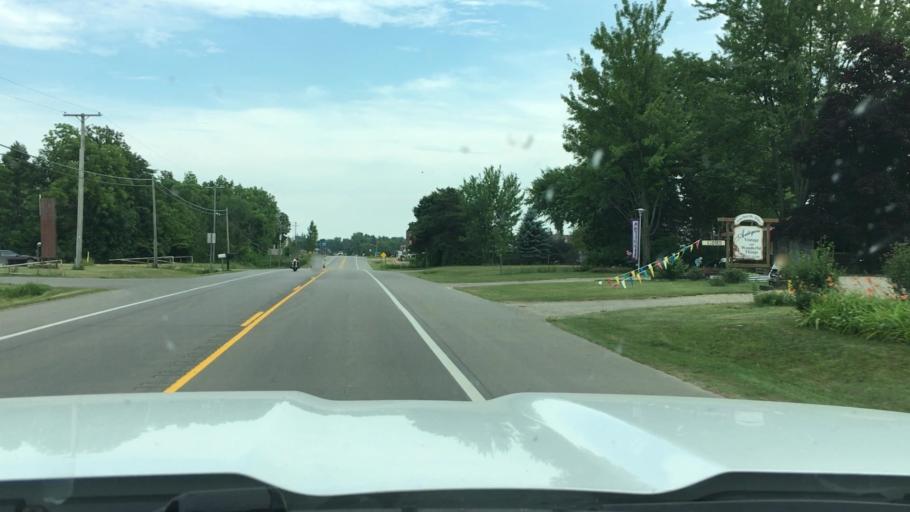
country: US
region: Michigan
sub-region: Sanilac County
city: Marlette
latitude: 43.3467
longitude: -83.0847
